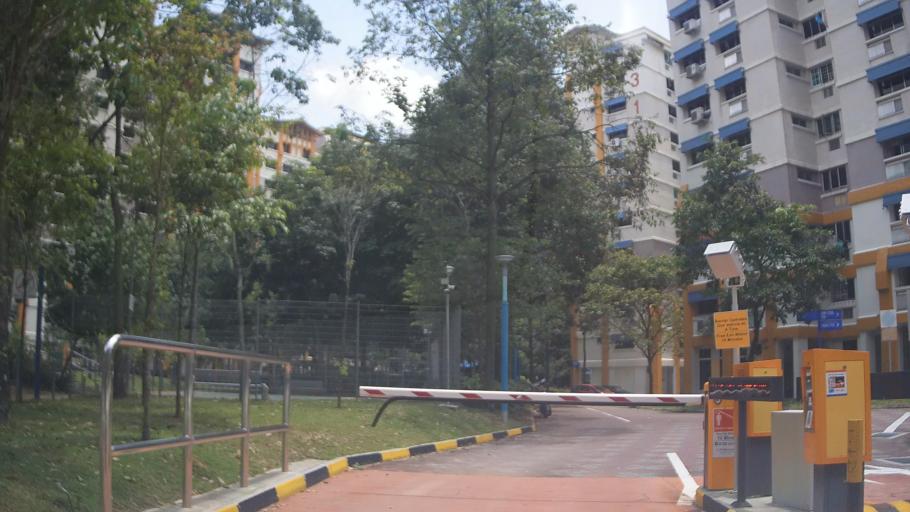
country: MY
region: Johor
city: Johor Bahru
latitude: 1.4423
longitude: 103.7971
